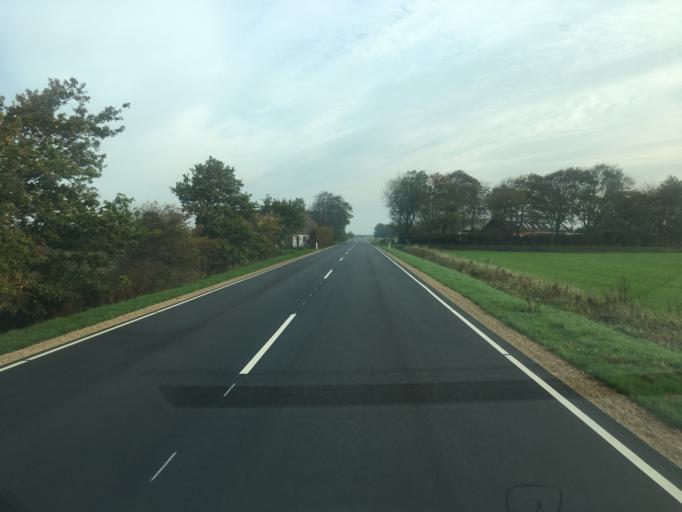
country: DK
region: South Denmark
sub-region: Tonder Kommune
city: Logumkloster
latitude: 55.0768
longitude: 8.9809
